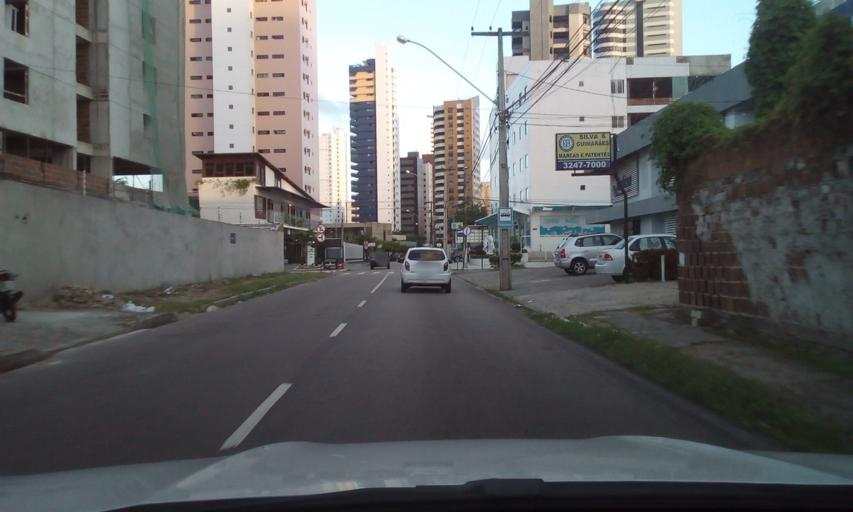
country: BR
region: Paraiba
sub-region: Joao Pessoa
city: Joao Pessoa
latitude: -7.1095
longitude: -34.8304
